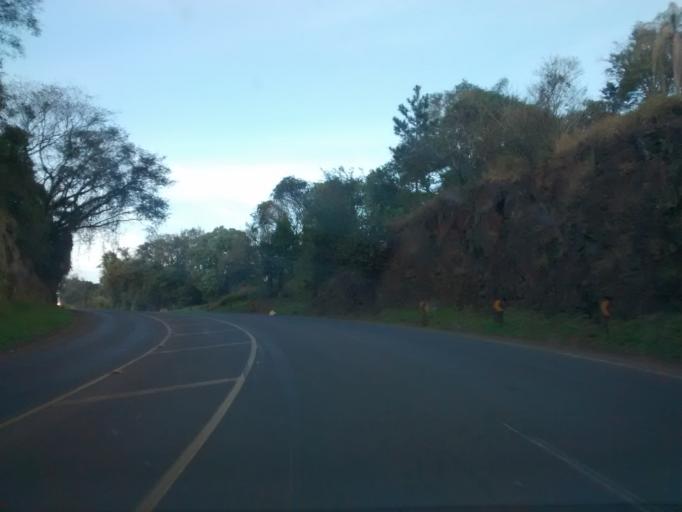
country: BR
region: Parana
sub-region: Francisco Beltrao
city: Francisco Beltrao
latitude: -26.1254
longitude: -53.0409
